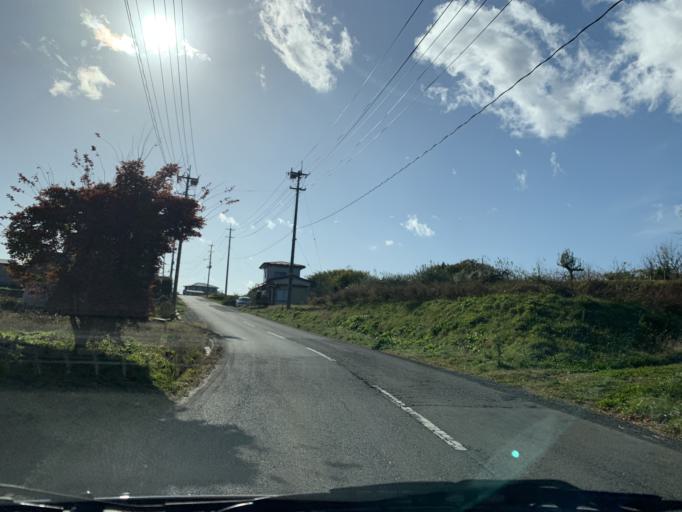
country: JP
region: Iwate
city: Mizusawa
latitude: 39.0610
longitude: 141.1190
